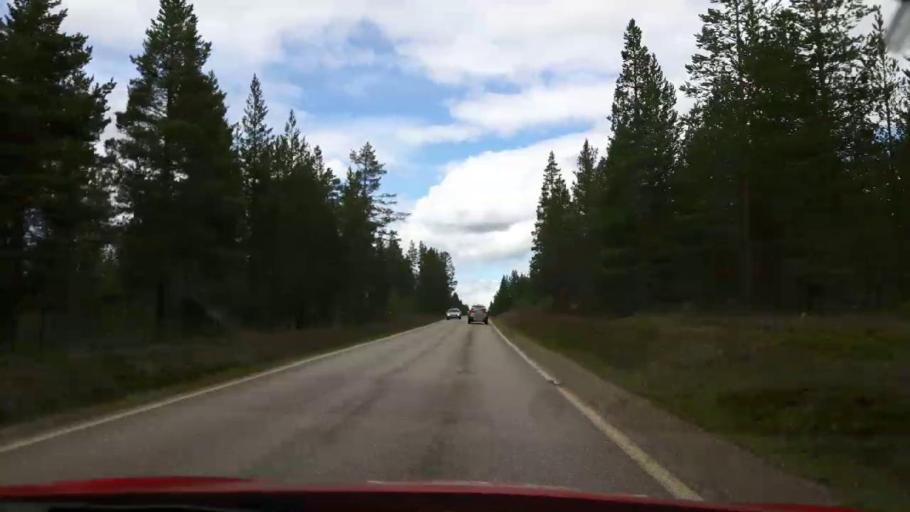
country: NO
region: Hedmark
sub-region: Trysil
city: Innbygda
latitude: 61.8427
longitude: 12.9556
